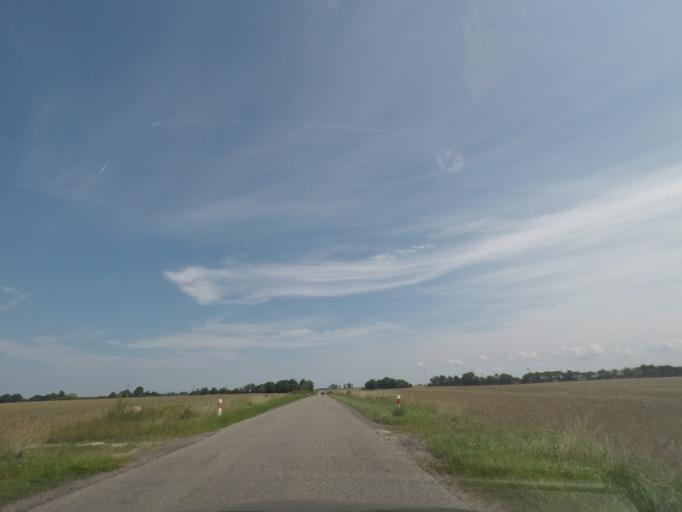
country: PL
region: Pomeranian Voivodeship
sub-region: Powiat slupski
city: Ustka
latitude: 54.5229
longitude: 16.7873
